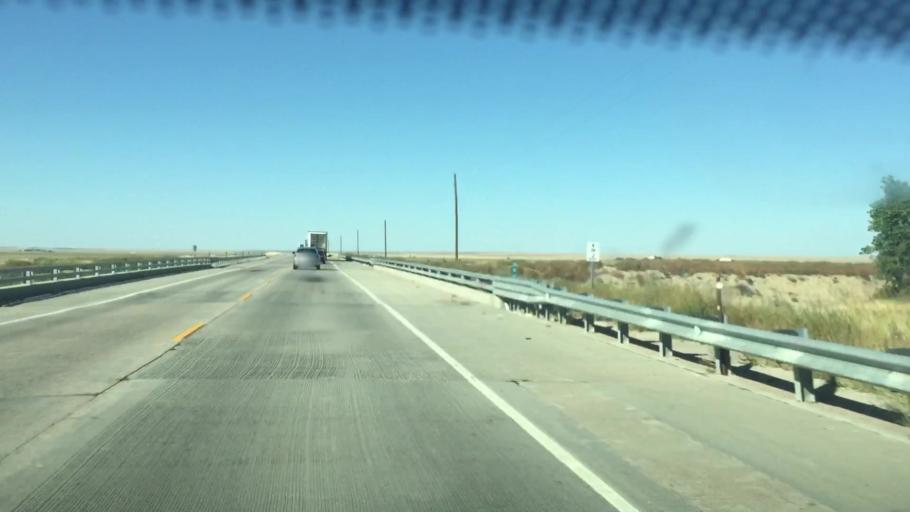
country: US
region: Colorado
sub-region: Kiowa County
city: Eads
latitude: 38.3327
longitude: -102.7198
